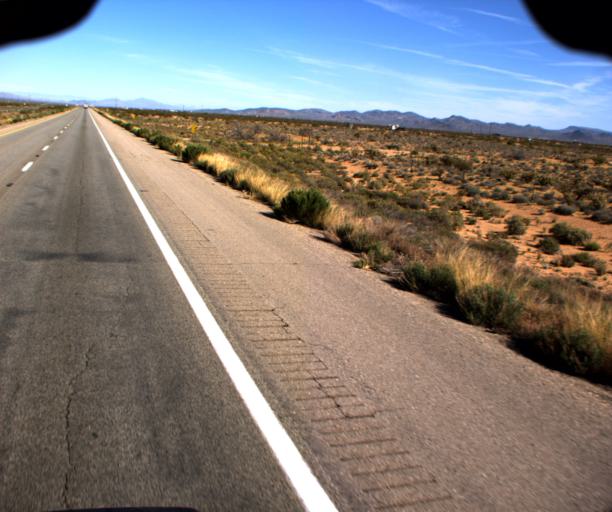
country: US
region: Arizona
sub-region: Mohave County
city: Dolan Springs
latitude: 35.4979
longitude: -114.3303
